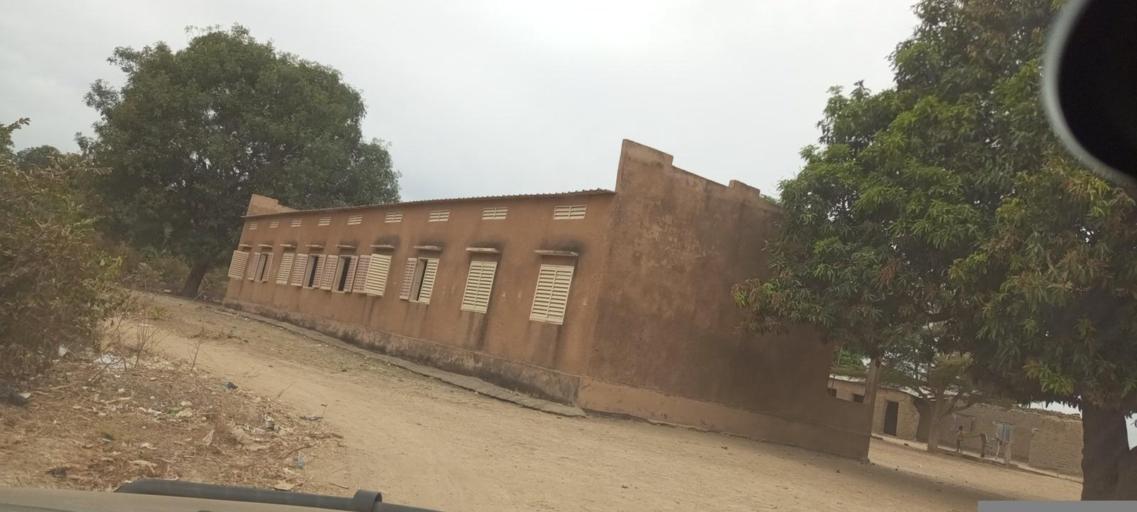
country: ML
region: Koulikoro
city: Kati
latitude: 12.7450
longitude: -8.3316
